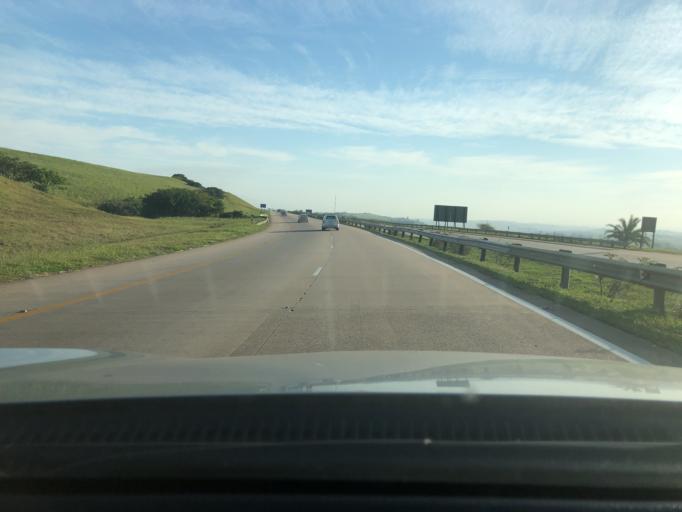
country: ZA
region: KwaZulu-Natal
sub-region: iLembe District Municipality
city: Stanger
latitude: -29.4378
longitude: 31.2641
